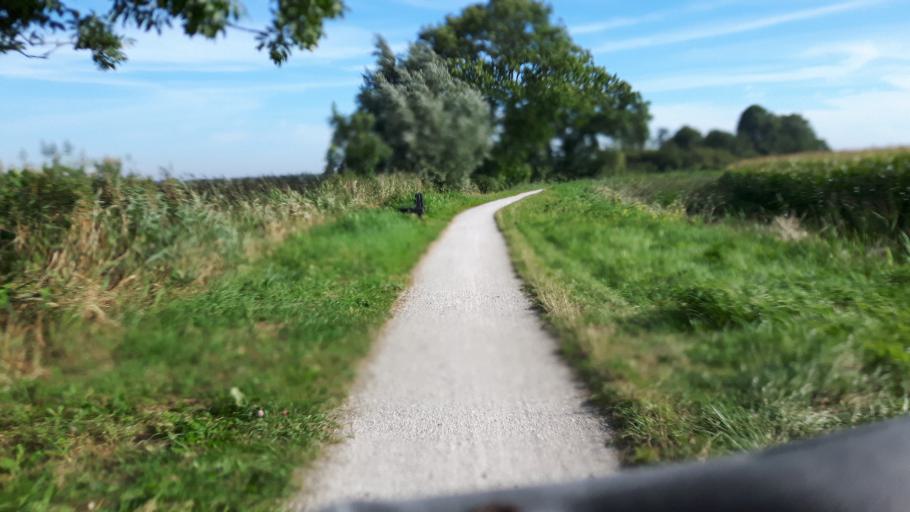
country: NL
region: Friesland
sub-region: Gemeente Skarsterlan
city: Sint Nicolaasga
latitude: 52.9672
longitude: 5.7503
